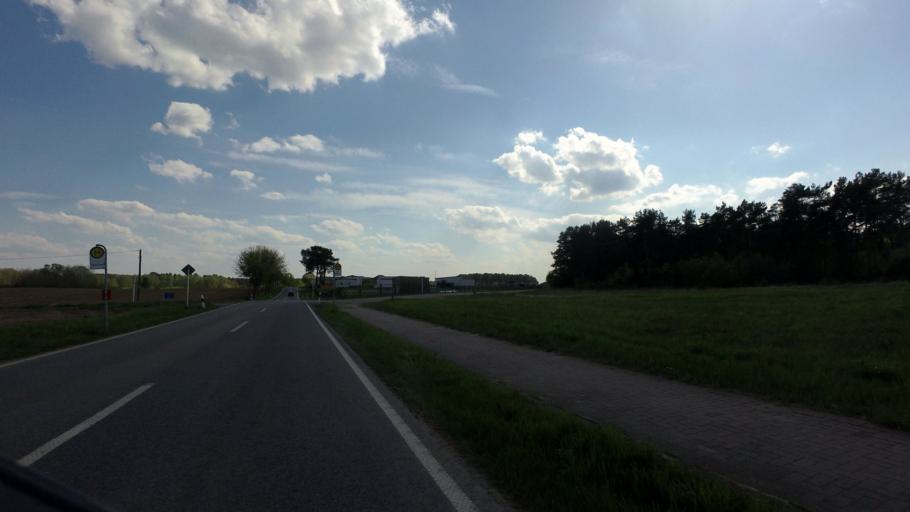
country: DE
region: Brandenburg
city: Templin
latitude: 53.1054
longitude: 13.5009
